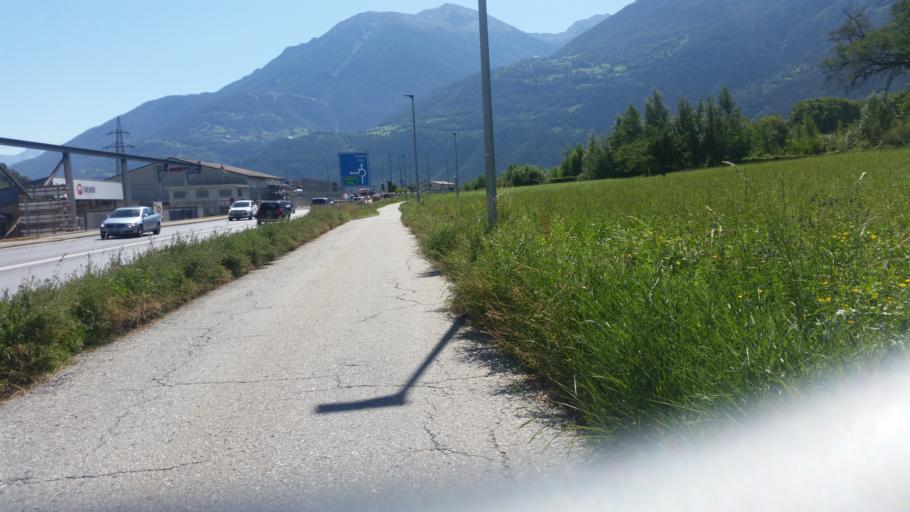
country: CH
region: Valais
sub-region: Leuk District
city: Leuk
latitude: 46.3098
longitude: 7.6488
